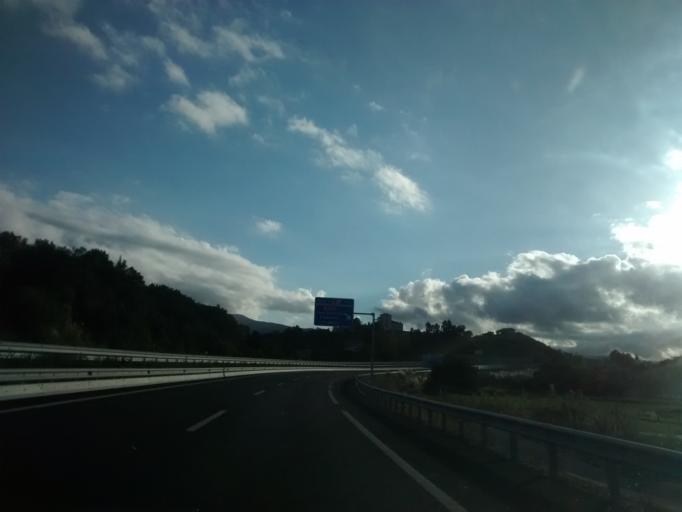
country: ES
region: Cantabria
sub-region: Provincia de Cantabria
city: Lierganes
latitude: 43.3790
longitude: -3.7489
